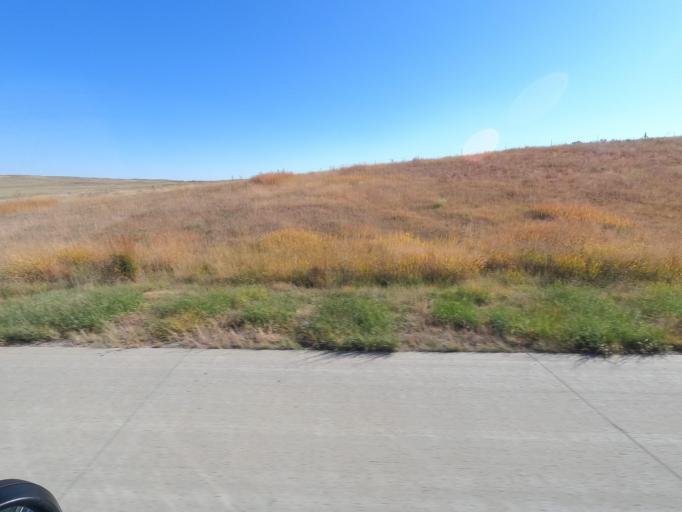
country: US
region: Nebraska
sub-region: Deuel County
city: Chappell
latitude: 40.9095
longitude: -102.4953
